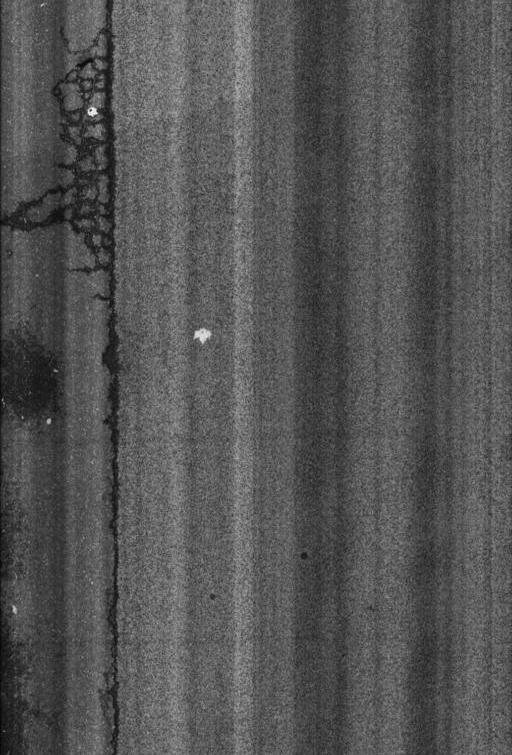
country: US
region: Maryland
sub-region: Prince George's County
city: Silver Hill
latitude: 38.8789
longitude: -76.9759
